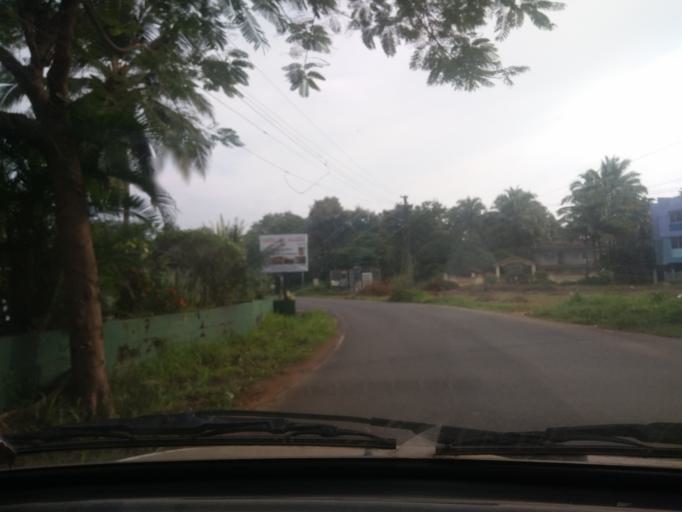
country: IN
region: Goa
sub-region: South Goa
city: Varca
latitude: 15.2228
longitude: 73.9444
